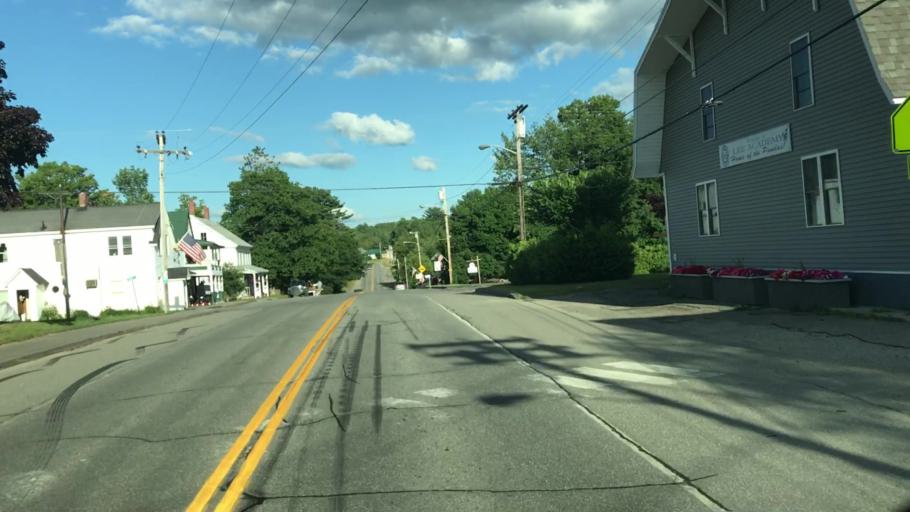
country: US
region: Maine
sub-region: Penobscot County
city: Lincoln
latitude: 45.3602
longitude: -68.2868
